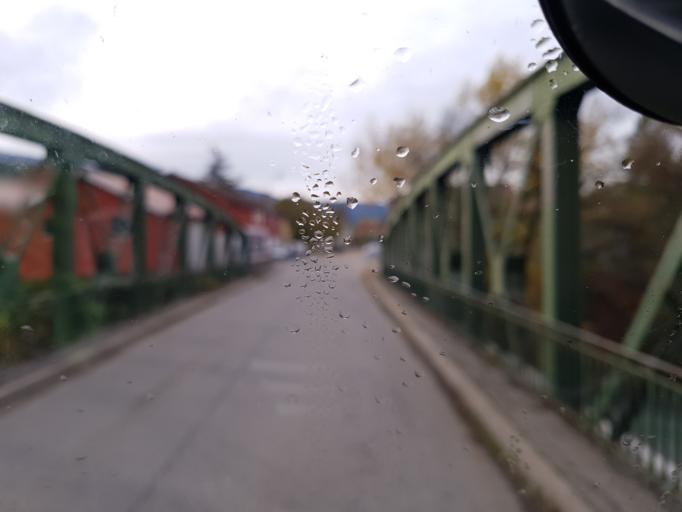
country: FR
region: Provence-Alpes-Cote d'Azur
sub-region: Departement des Hautes-Alpes
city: Laragne-Monteglin
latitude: 44.3447
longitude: 5.7700
